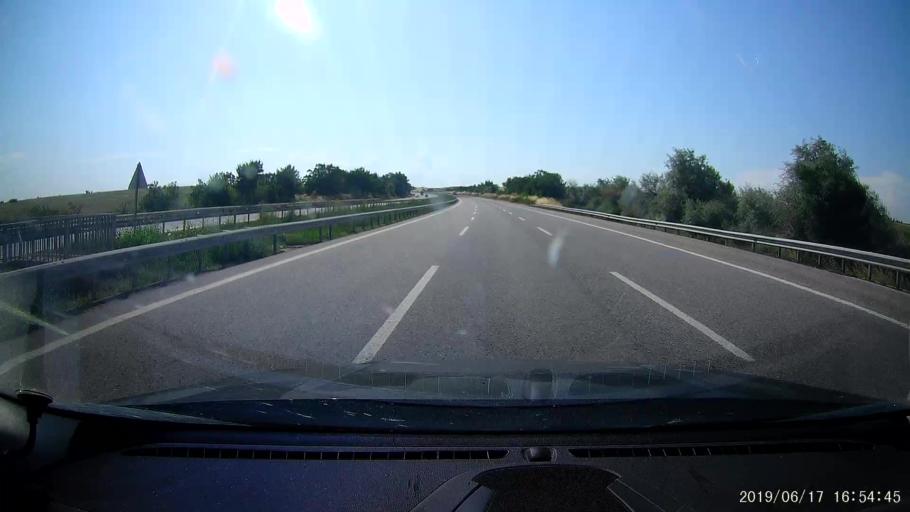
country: TR
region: Kirklareli
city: Inece
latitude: 41.5764
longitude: 26.9866
